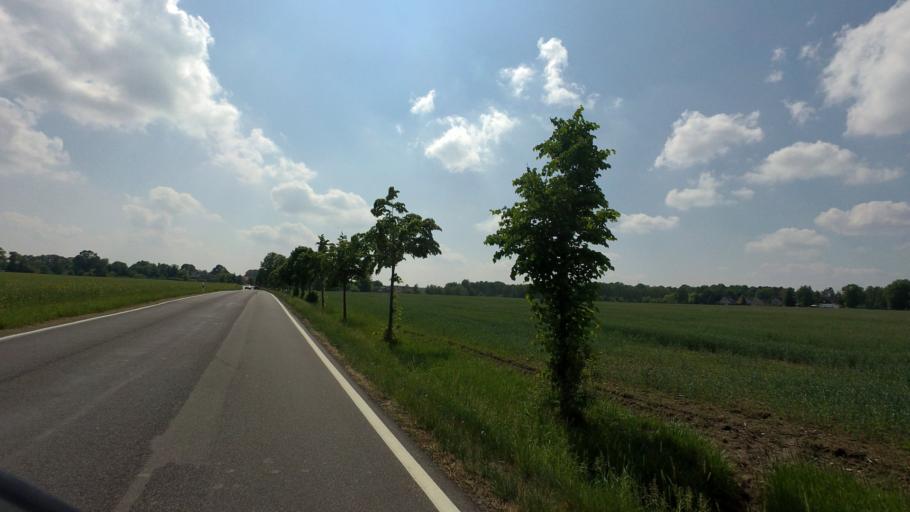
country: DE
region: Saxony
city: Mucka
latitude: 51.2735
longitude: 14.6496
